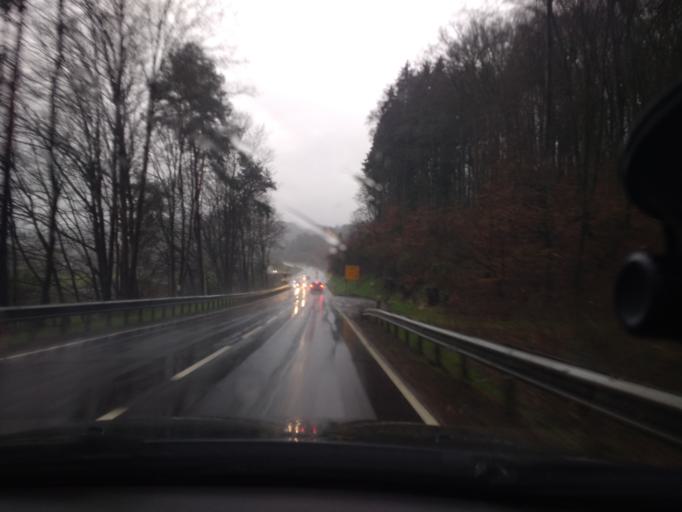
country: DE
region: Rheinland-Pfalz
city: Tawern
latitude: 49.6552
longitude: 6.5299
